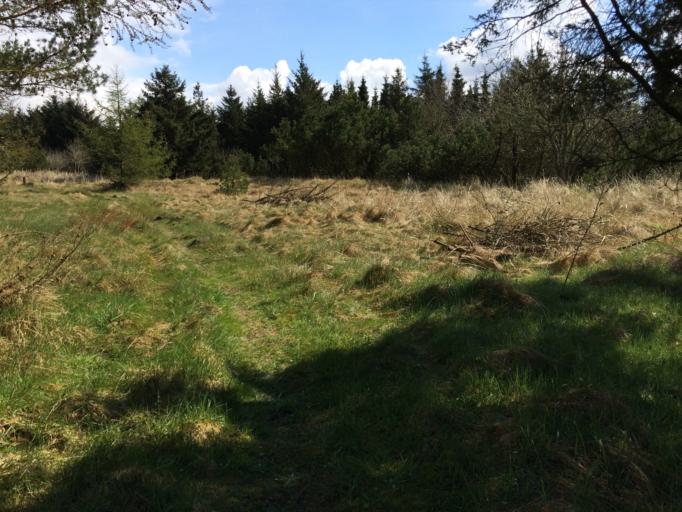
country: DK
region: Central Jutland
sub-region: Holstebro Kommune
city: Ulfborg
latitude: 56.2397
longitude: 8.3919
